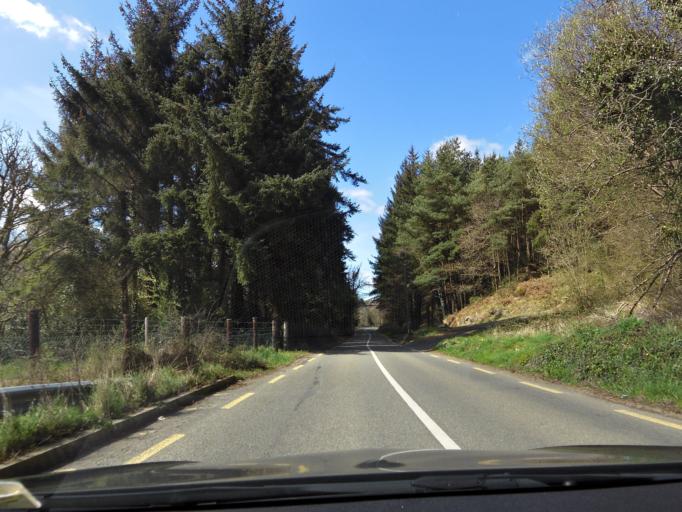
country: IE
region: Leinster
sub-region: Wicklow
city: Aughrim
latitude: 52.8470
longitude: -6.2725
